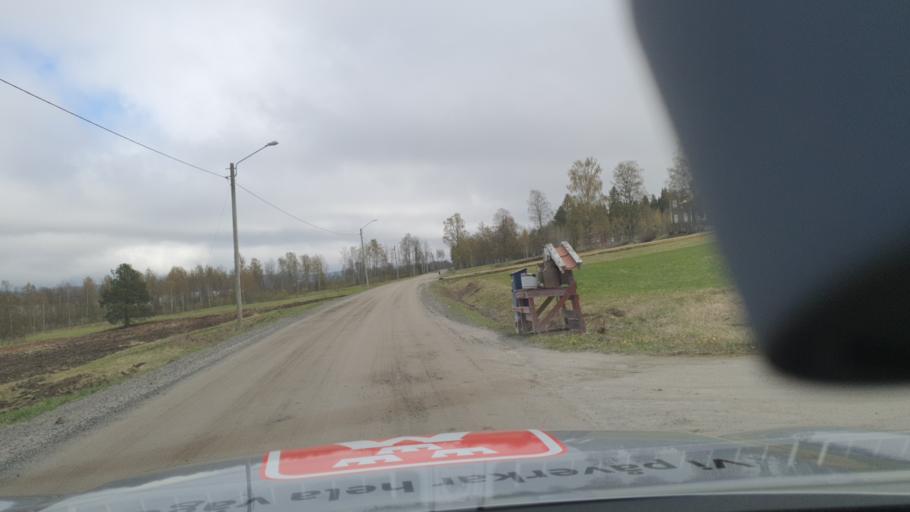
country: SE
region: Vaesterbotten
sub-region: Bjurholms Kommun
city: Bjurholm
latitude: 63.6648
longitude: 19.0177
